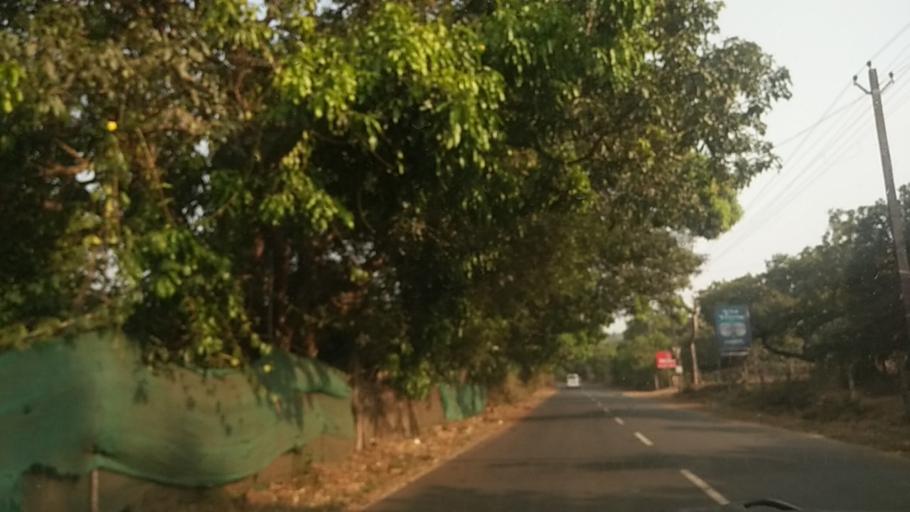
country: IN
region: Goa
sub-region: North Goa
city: Morjim
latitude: 15.6548
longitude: 73.7527
